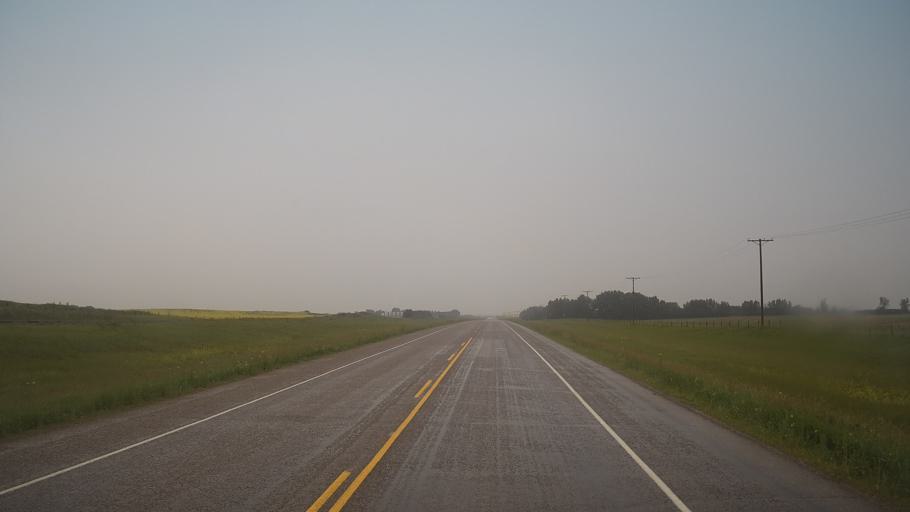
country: CA
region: Saskatchewan
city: Biggar
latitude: 52.1334
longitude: -108.1585
